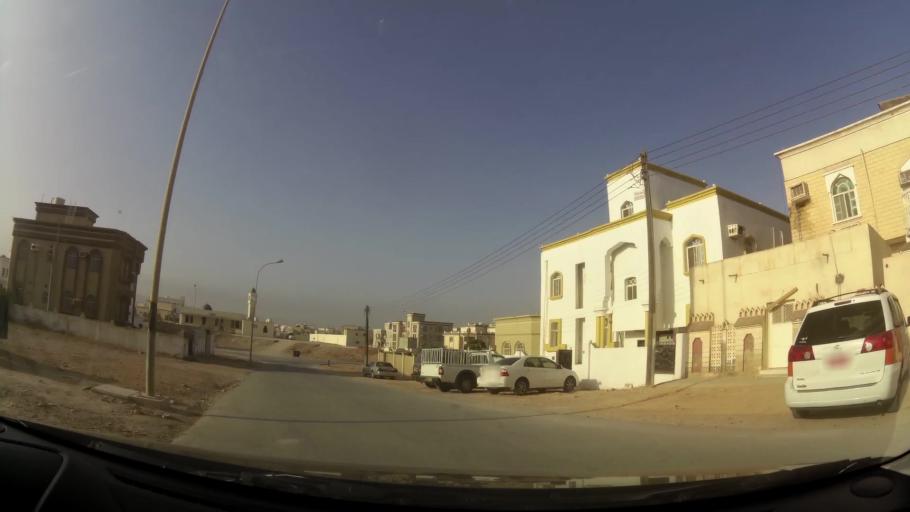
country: OM
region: Zufar
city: Salalah
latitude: 17.0126
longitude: 54.0321
